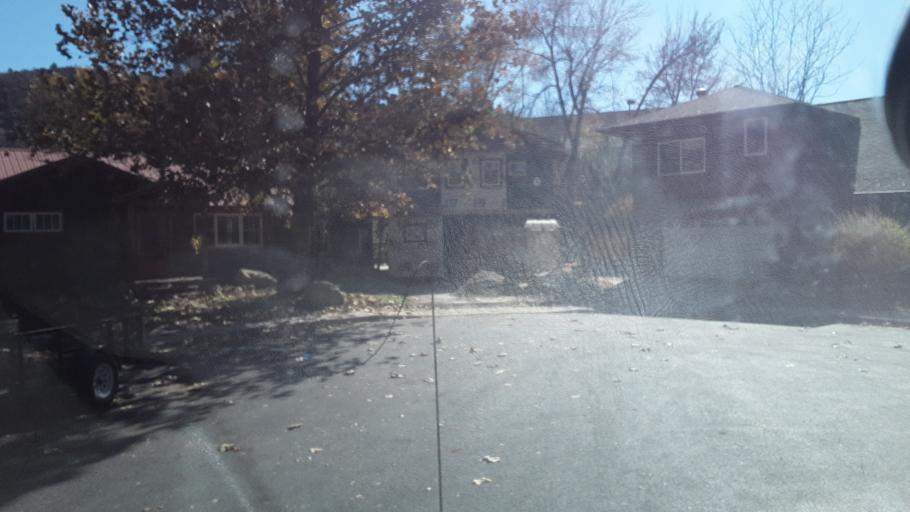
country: US
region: Colorado
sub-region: La Plata County
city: Durango
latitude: 37.2850
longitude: -107.8731
